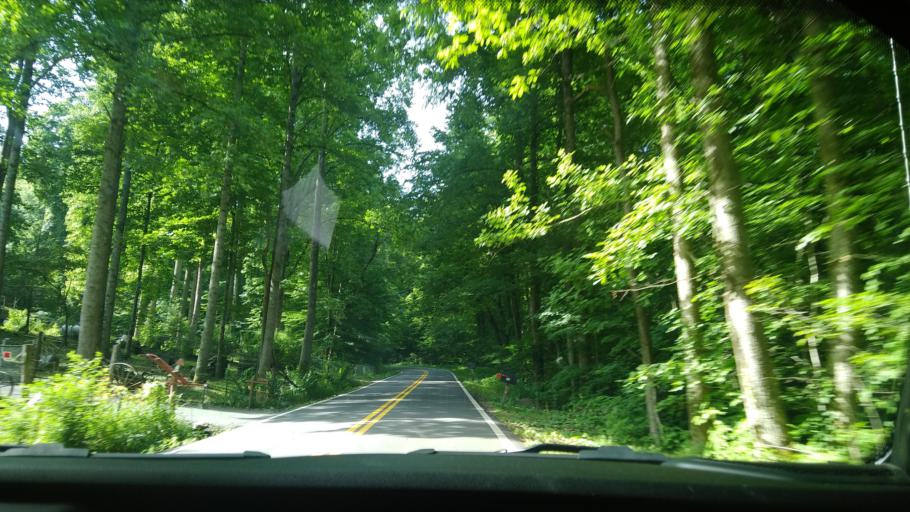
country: US
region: Tennessee
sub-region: Cocke County
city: Newport
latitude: 35.7834
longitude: -83.1909
